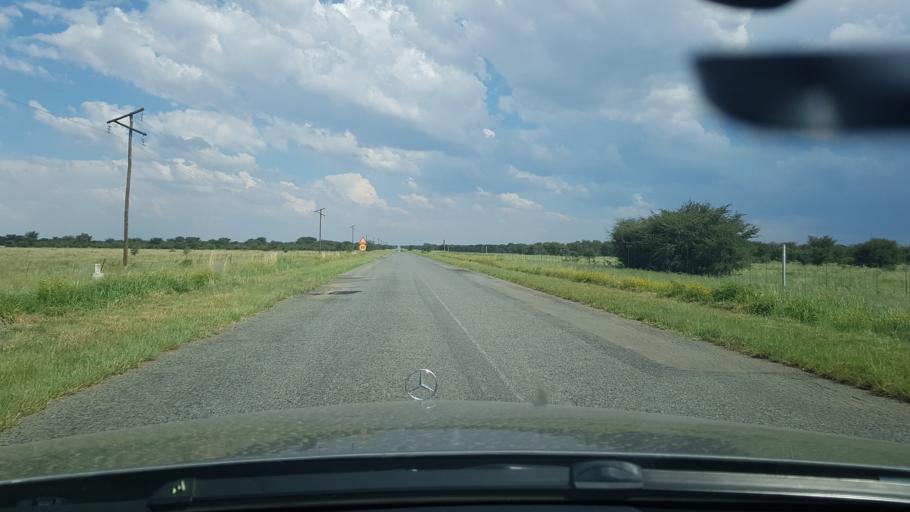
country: ZA
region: North-West
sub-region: Dr Ruth Segomotsi Mompati District Municipality
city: Bloemhof
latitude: -27.7665
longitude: 25.6012
